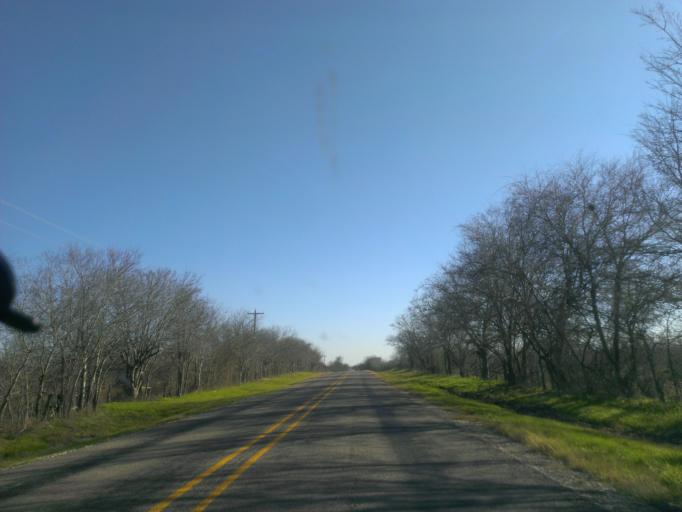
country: US
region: Texas
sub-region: Bastrop County
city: Elgin
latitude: 30.4663
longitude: -97.2726
